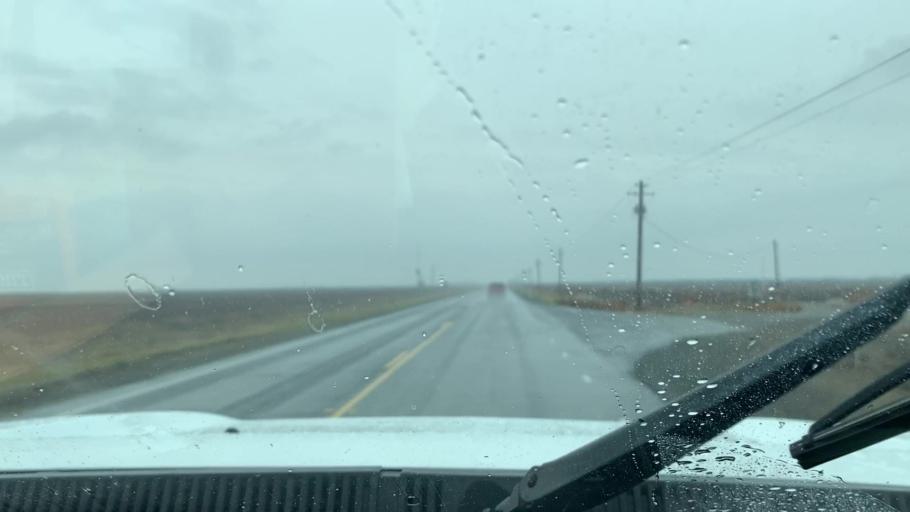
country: US
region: California
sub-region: Tulare County
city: Alpaugh
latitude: 35.9241
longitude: -119.4292
